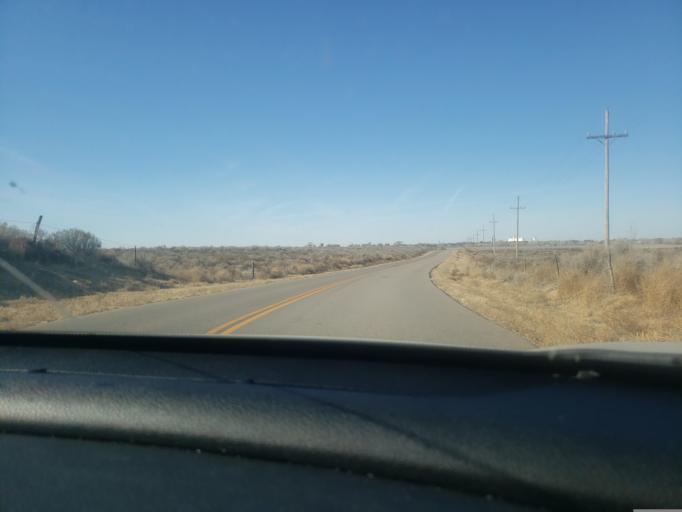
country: US
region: Kansas
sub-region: Finney County
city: Garden City
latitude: 37.9479
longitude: -100.8497
